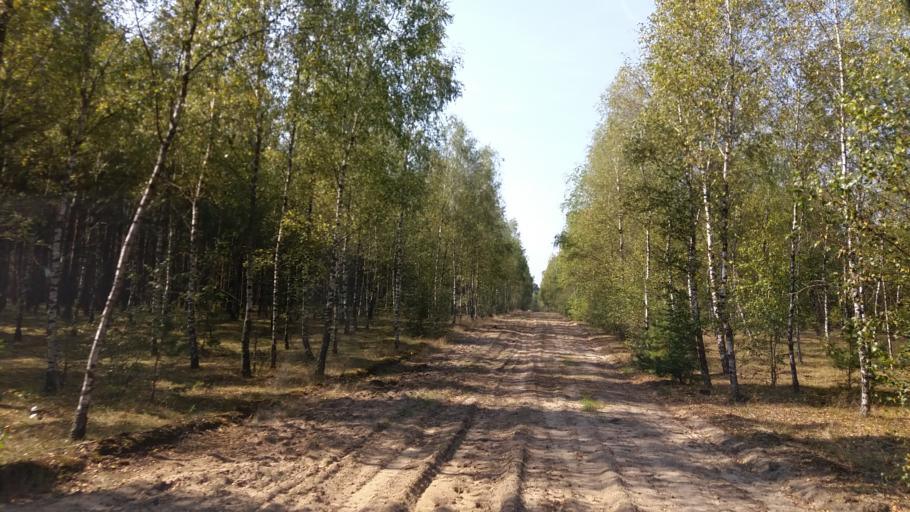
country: PL
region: West Pomeranian Voivodeship
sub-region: Powiat drawski
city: Kalisz Pomorski
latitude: 53.1991
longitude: 15.9813
